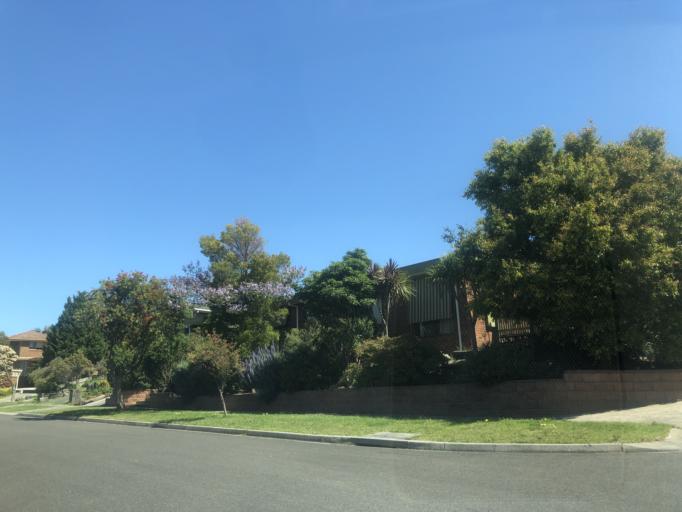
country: AU
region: Victoria
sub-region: Casey
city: Endeavour Hills
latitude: -37.9850
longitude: 145.2709
